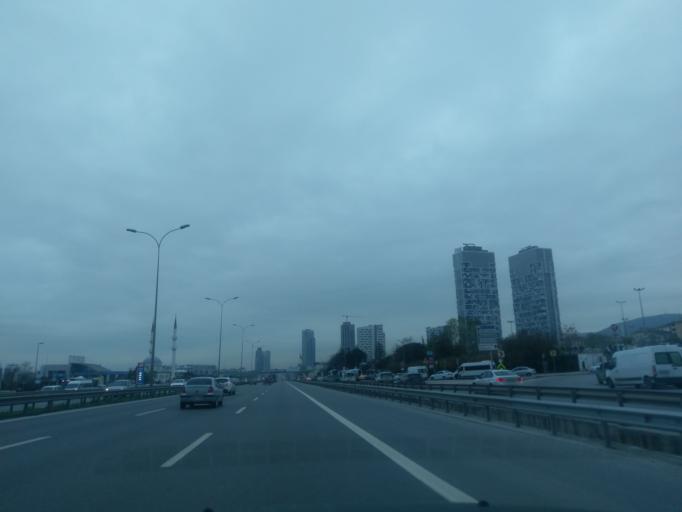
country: TR
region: Istanbul
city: Maltepe
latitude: 40.9119
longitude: 29.1944
